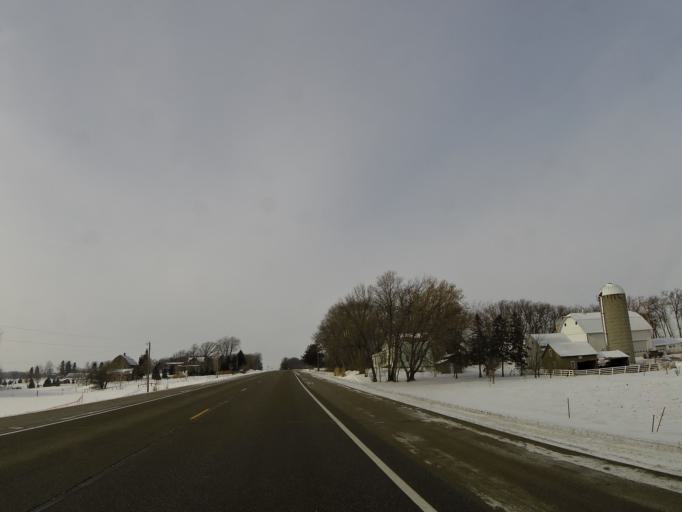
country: US
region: Minnesota
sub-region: Hennepin County
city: Saint Bonifacius
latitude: 44.9053
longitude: -93.7997
